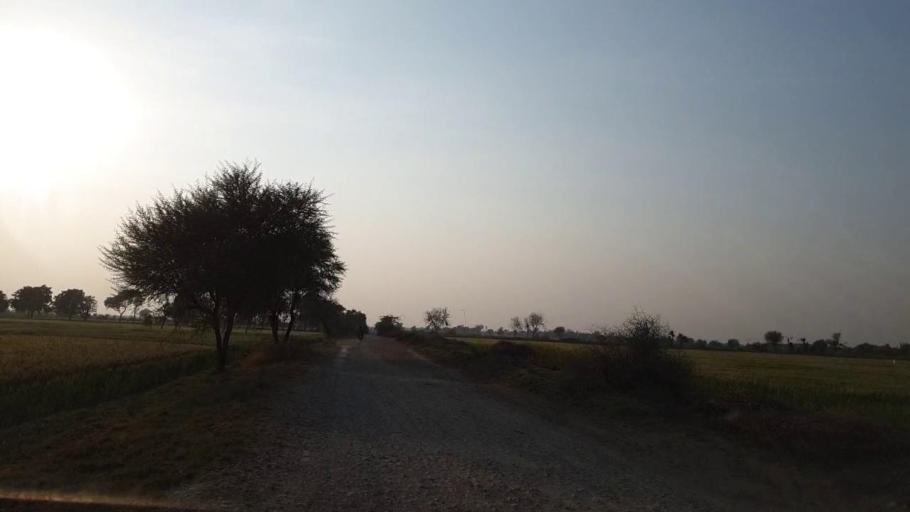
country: PK
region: Sindh
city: Pithoro
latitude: 25.6541
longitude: 69.2271
